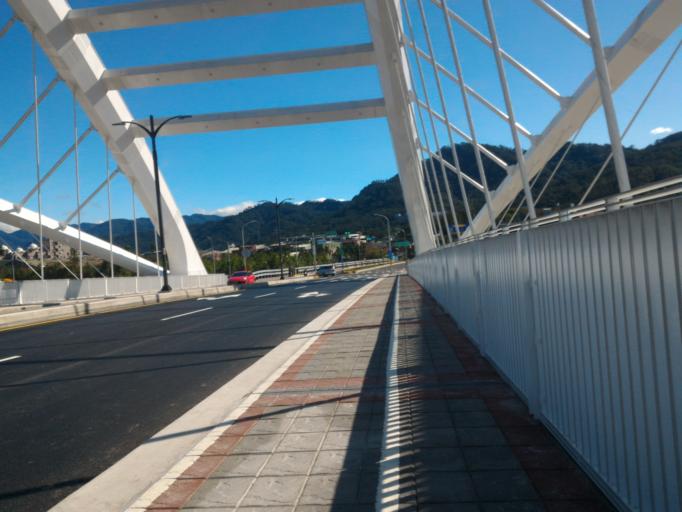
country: TW
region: Taiwan
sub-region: Taoyuan
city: Taoyuan
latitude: 24.9370
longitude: 121.3888
